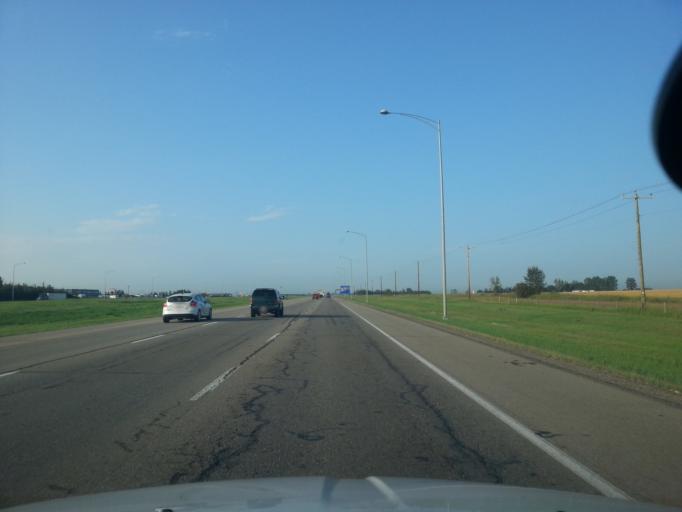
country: CA
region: Alberta
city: Leduc
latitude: 53.3559
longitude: -113.5390
